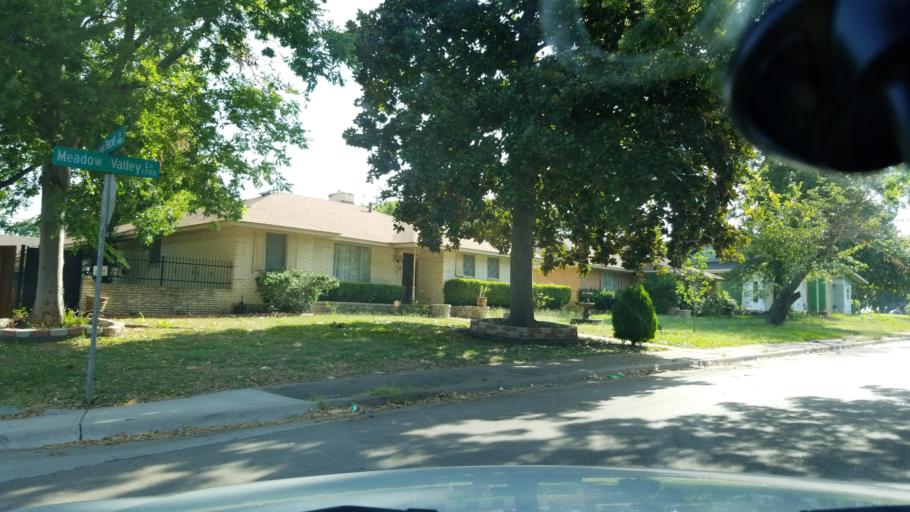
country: US
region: Texas
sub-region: Dallas County
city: Duncanville
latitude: 32.6739
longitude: -96.8498
